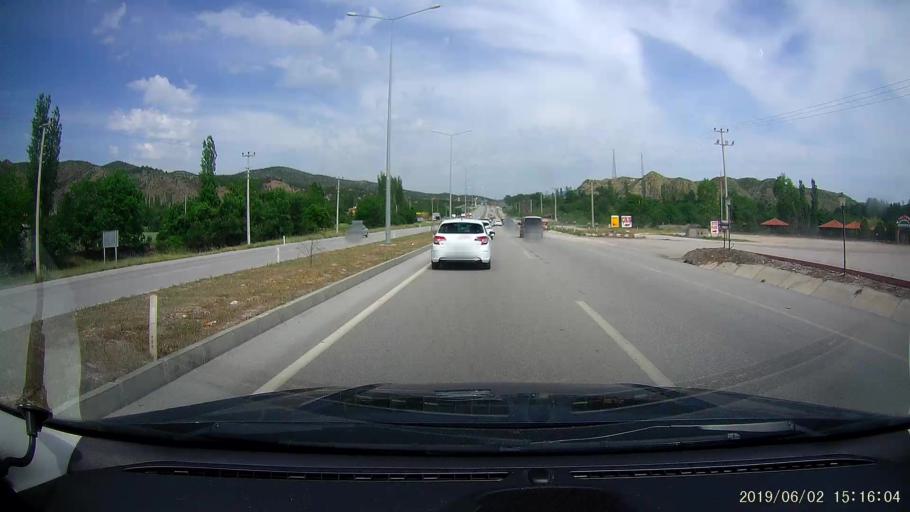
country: TR
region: Corum
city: Osmancik
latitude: 40.9702
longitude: 34.8591
